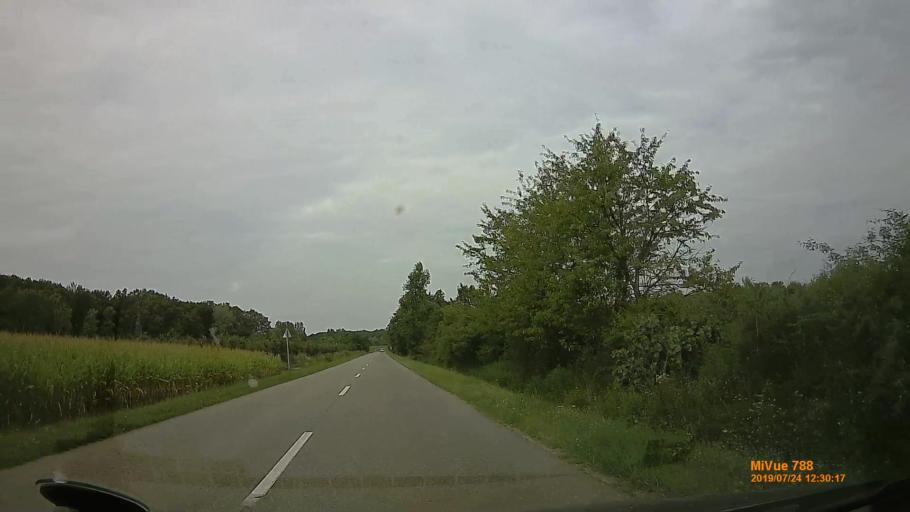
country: HU
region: Szabolcs-Szatmar-Bereg
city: Vasarosnameny
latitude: 48.1635
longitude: 22.3398
